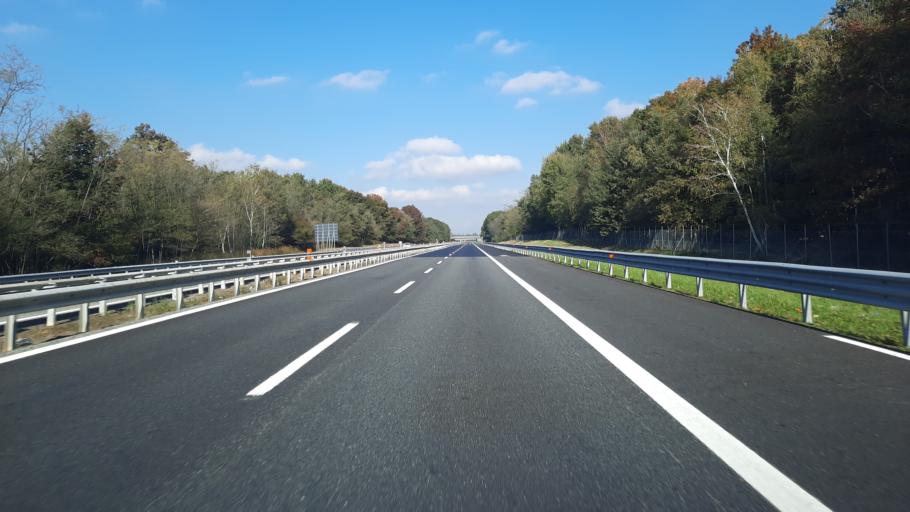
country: IT
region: Piedmont
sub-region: Provincia di Novara
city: Fontaneto D'Agogna
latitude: 45.6318
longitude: 8.4508
